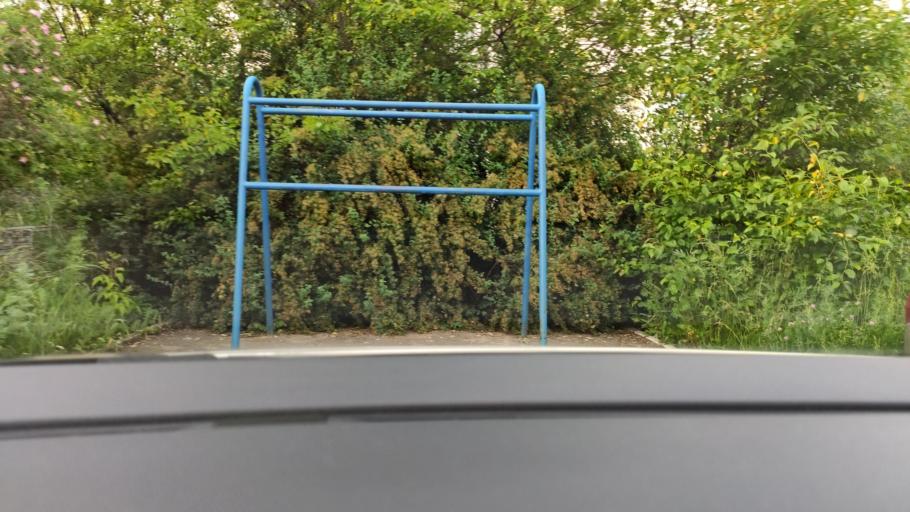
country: RU
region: Voronezj
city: Novaya Usman'
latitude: 51.6078
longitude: 39.3697
